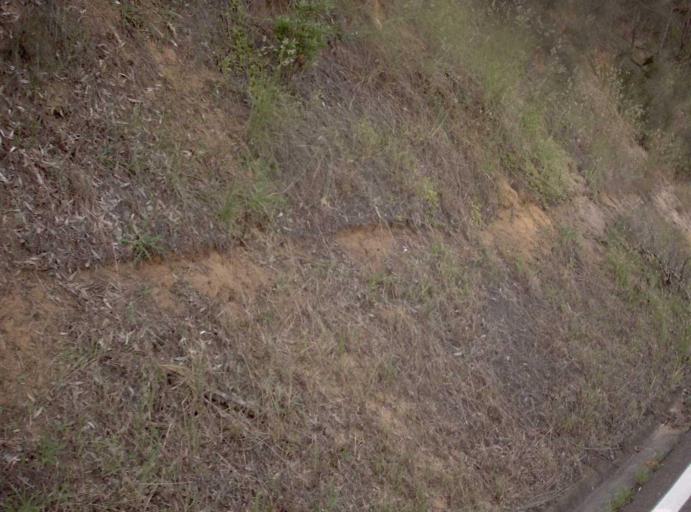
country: AU
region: Victoria
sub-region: East Gippsland
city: Lakes Entrance
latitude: -37.8810
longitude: 147.9659
